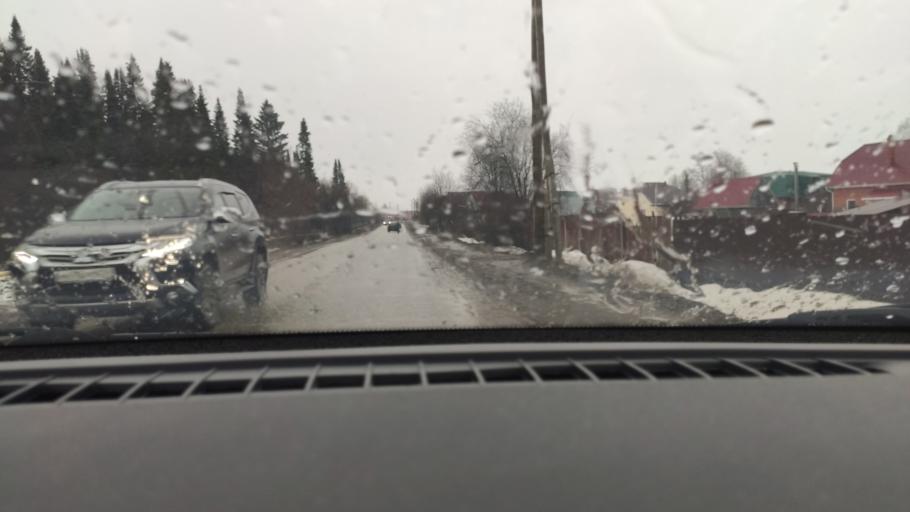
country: RU
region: Perm
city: Kultayevo
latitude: 57.9001
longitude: 55.9527
